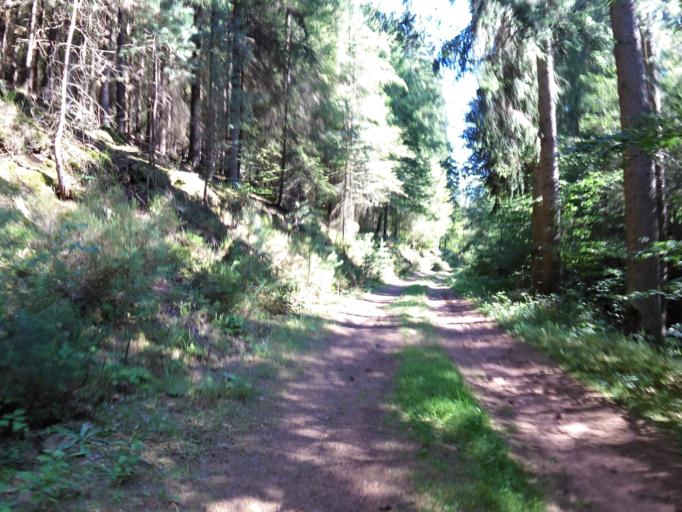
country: DE
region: Rheinland-Pfalz
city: Esthal
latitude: 49.3744
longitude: 7.9742
